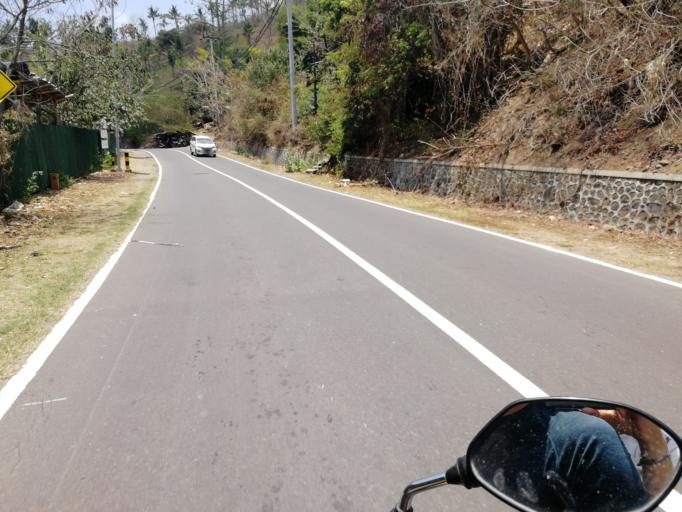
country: ID
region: West Nusa Tenggara
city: Karangsubagan
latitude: -8.4465
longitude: 116.0339
